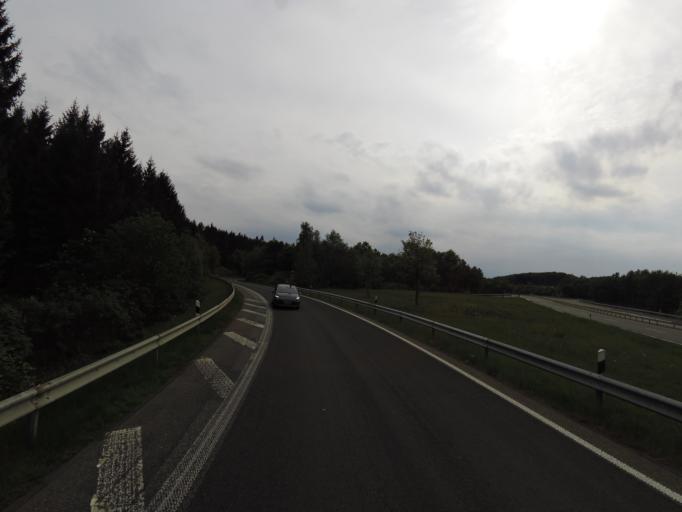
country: DE
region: Rheinland-Pfalz
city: Nortershausen
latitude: 50.2463
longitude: 7.5179
